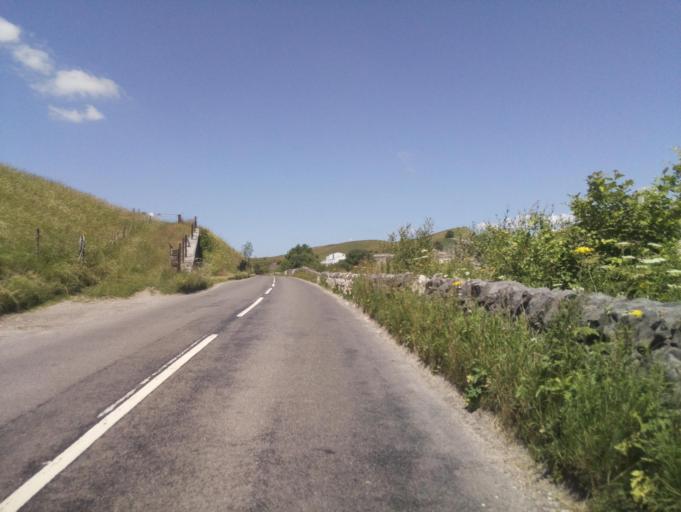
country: GB
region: England
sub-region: Derbyshire
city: Buxton
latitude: 53.2900
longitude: -1.8656
